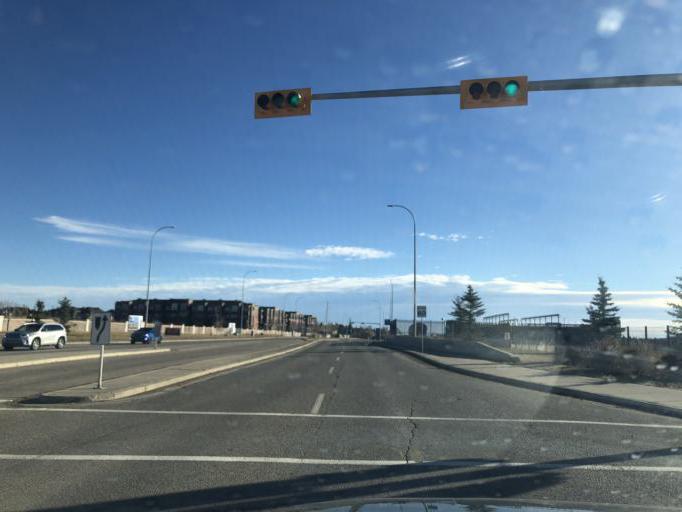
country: CA
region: Alberta
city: Calgary
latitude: 51.0377
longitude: -114.1936
